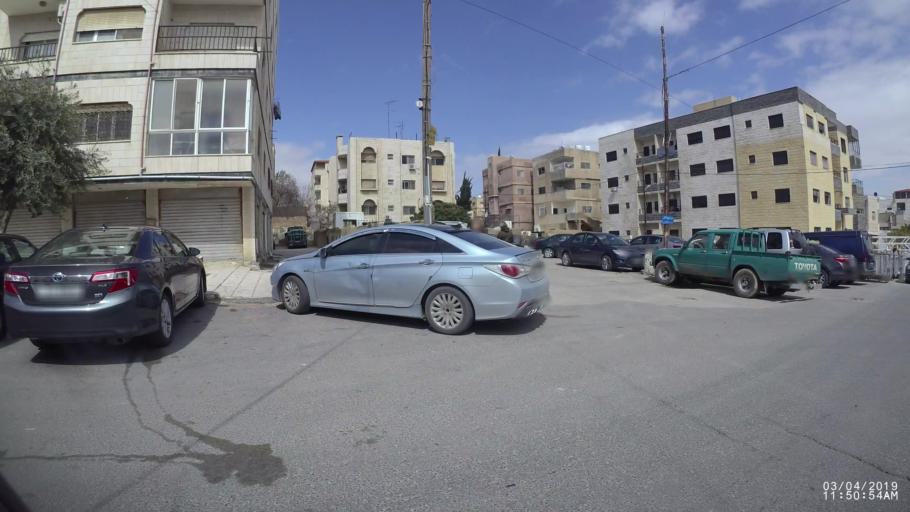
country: JO
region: Amman
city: Wadi as Sir
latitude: 31.9554
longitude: 35.8406
